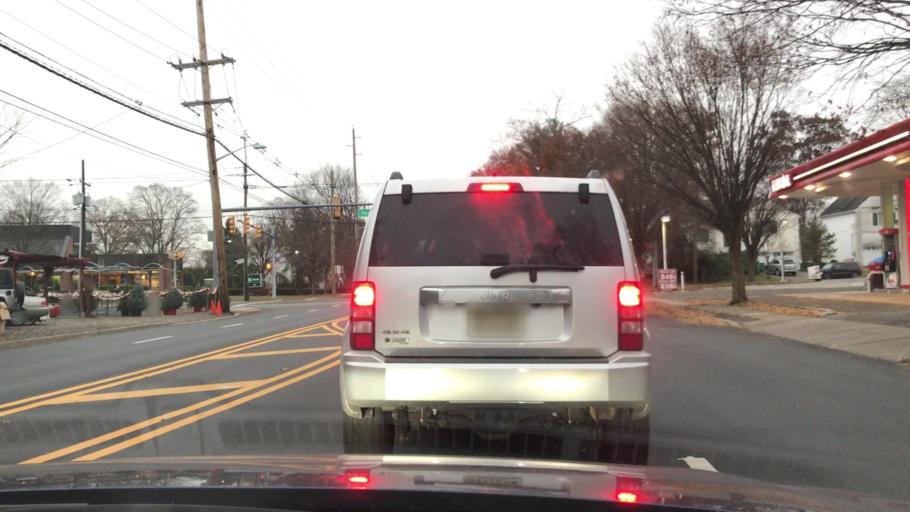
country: US
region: New Jersey
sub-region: Bergen County
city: Ridgewood
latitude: 40.9723
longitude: -74.0914
